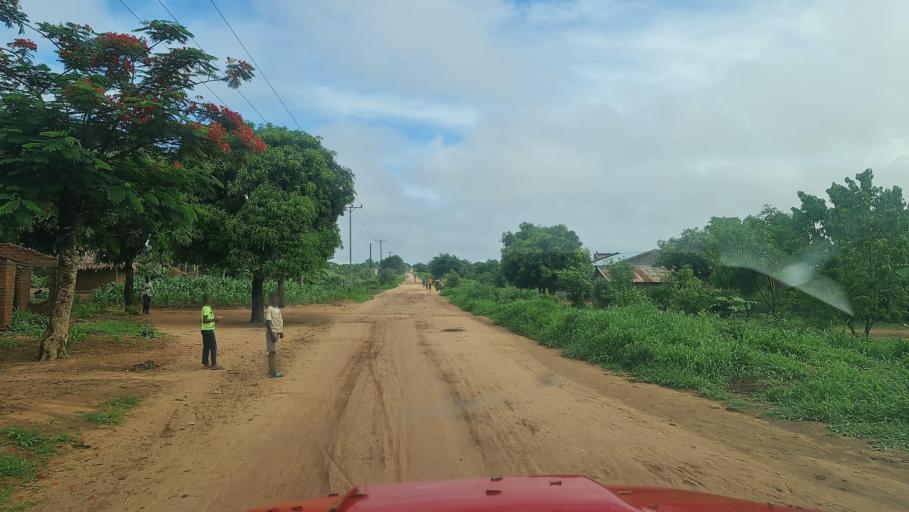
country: MW
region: Southern Region
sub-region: Nsanje District
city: Nsanje
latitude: -17.3162
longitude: 35.5923
